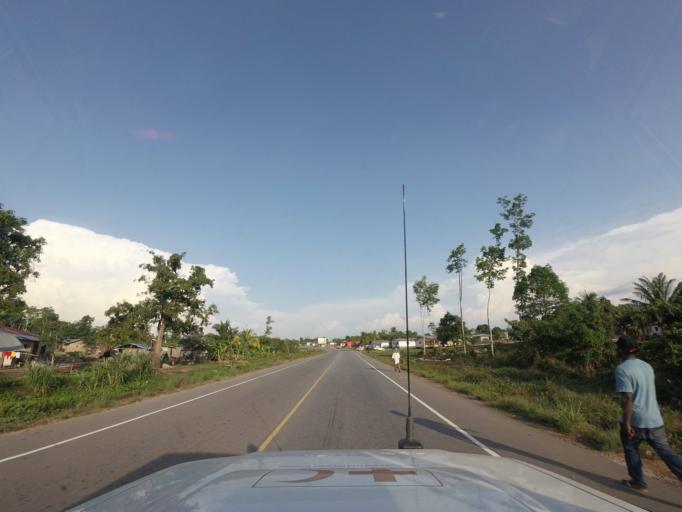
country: LR
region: Bong
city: Gbarnga
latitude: 7.0022
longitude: -9.2925
